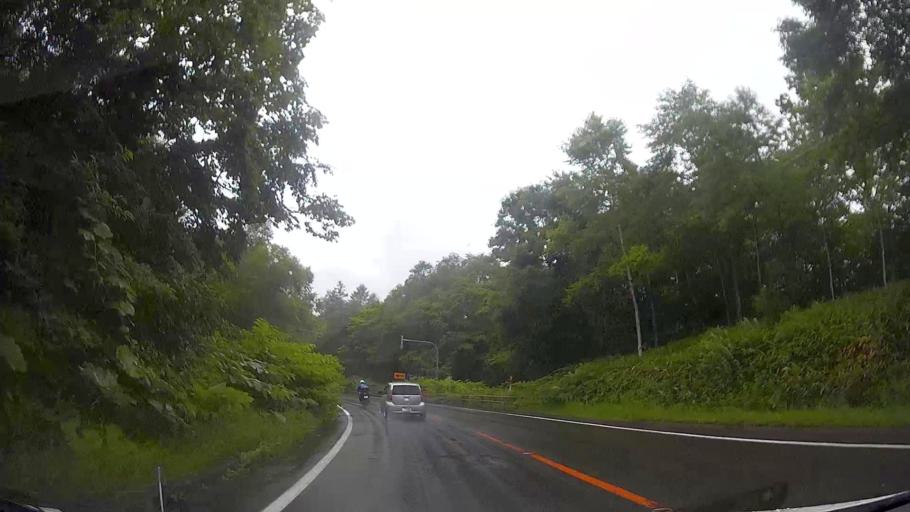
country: JP
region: Hokkaido
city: Shiraoi
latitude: 42.7180
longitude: 141.2222
